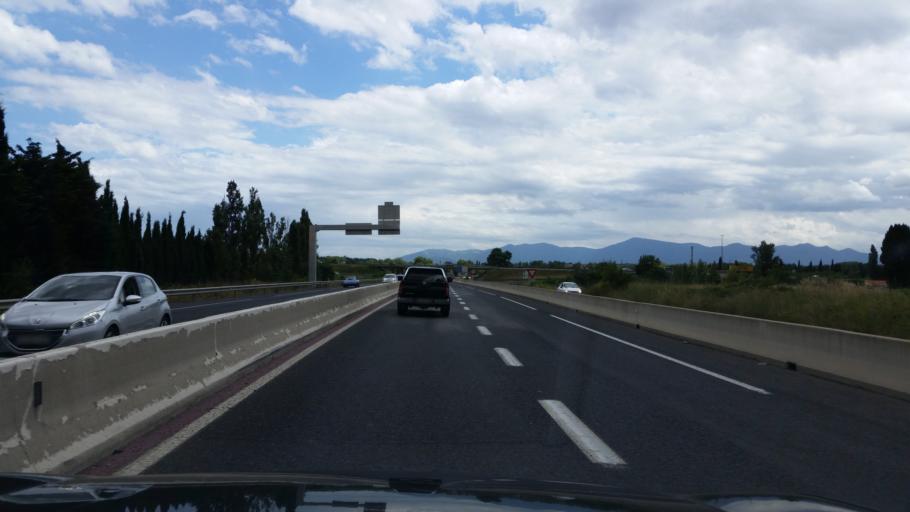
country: FR
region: Languedoc-Roussillon
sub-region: Departement des Pyrenees-Orientales
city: Toulouges
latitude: 42.6739
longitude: 2.8554
